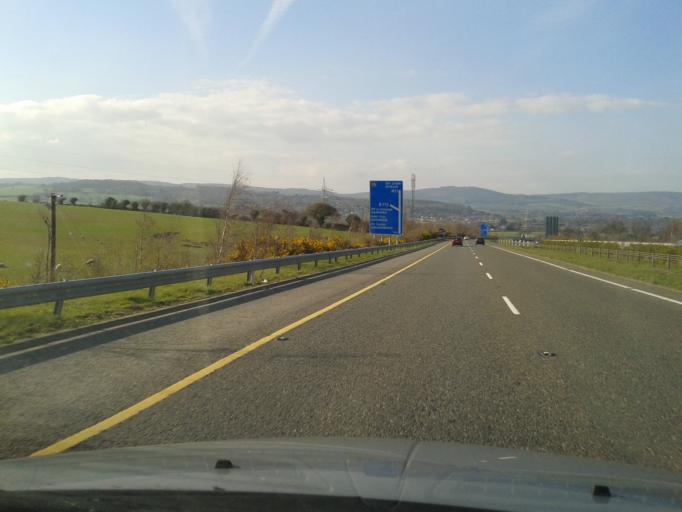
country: IE
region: Leinster
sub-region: Wicklow
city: Rathnew
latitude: 52.9878
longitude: -6.0923
